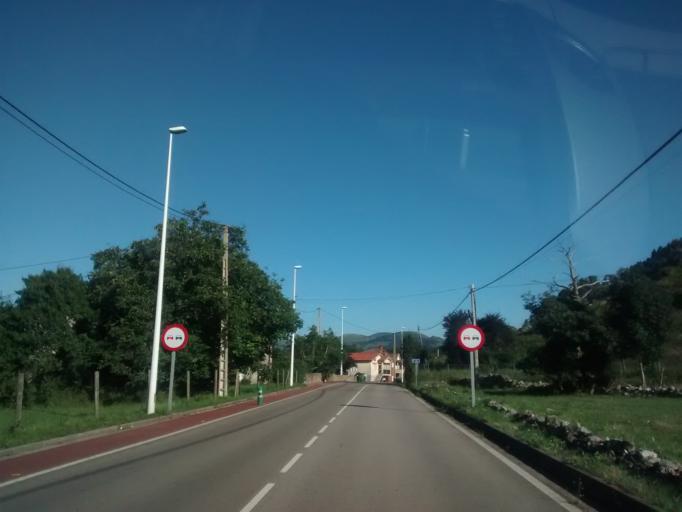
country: ES
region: Cantabria
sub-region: Provincia de Cantabria
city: Entrambasaguas
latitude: 43.3870
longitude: -3.6976
